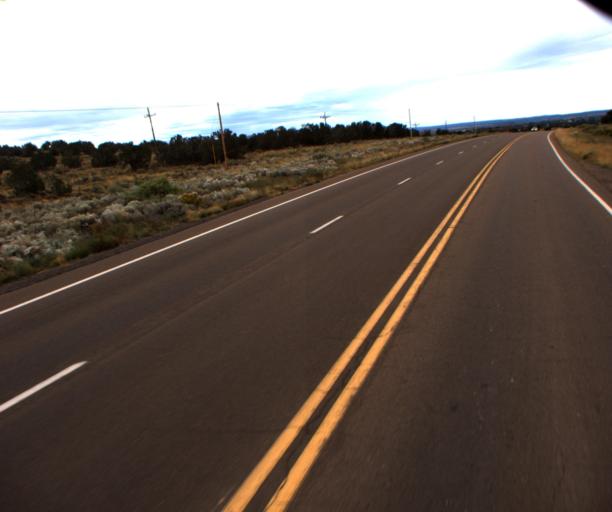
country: US
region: Arizona
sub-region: Navajo County
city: Snowflake
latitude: 34.5435
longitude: -110.0794
